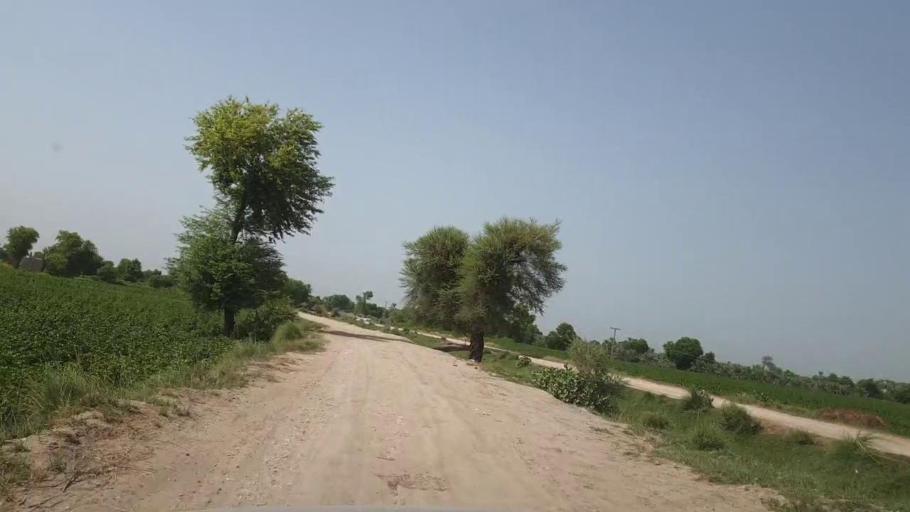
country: PK
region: Sindh
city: Pano Aqil
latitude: 27.8350
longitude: 69.1853
